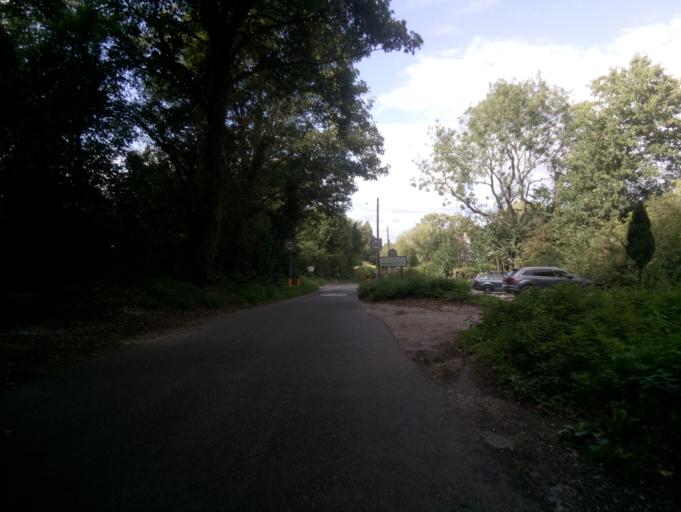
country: GB
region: England
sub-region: Hampshire
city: Chandlers Ford
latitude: 51.0726
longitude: -1.3805
